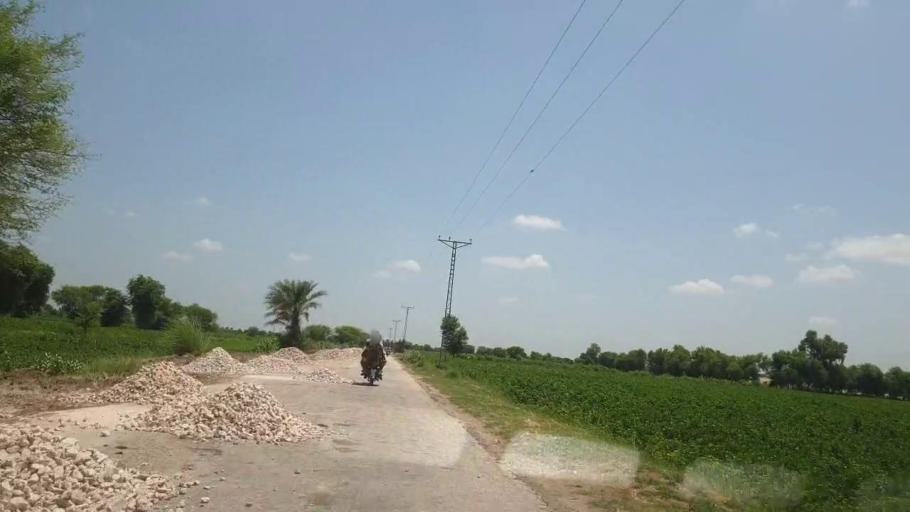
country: PK
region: Sindh
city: Pano Aqil
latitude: 27.6661
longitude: 69.2126
